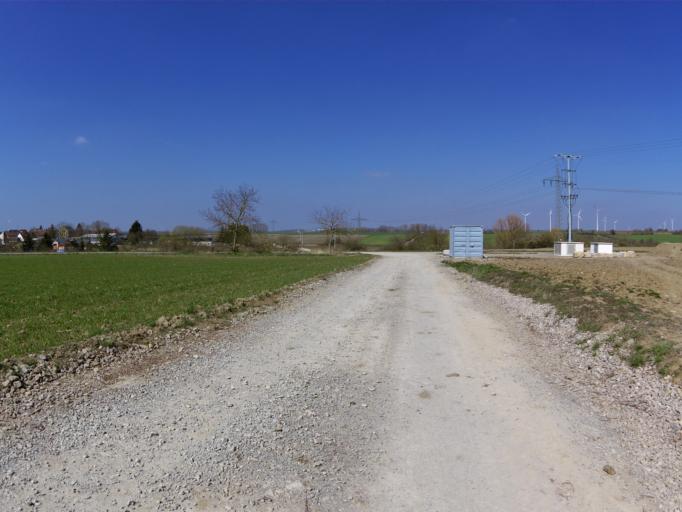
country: DE
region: Bavaria
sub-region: Regierungsbezirk Unterfranken
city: Biebelried
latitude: 49.7299
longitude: 10.0955
